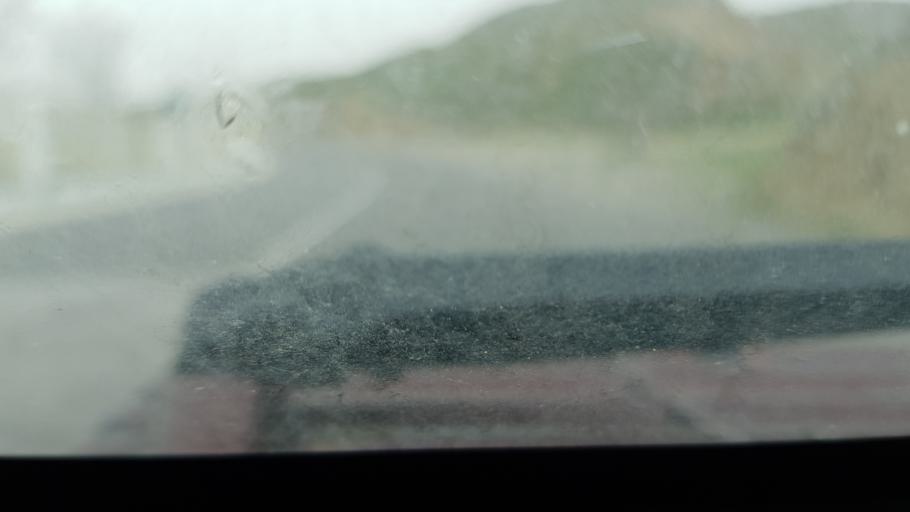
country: TM
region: Ahal
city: Arcabil
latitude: 38.0405
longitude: 58.0129
